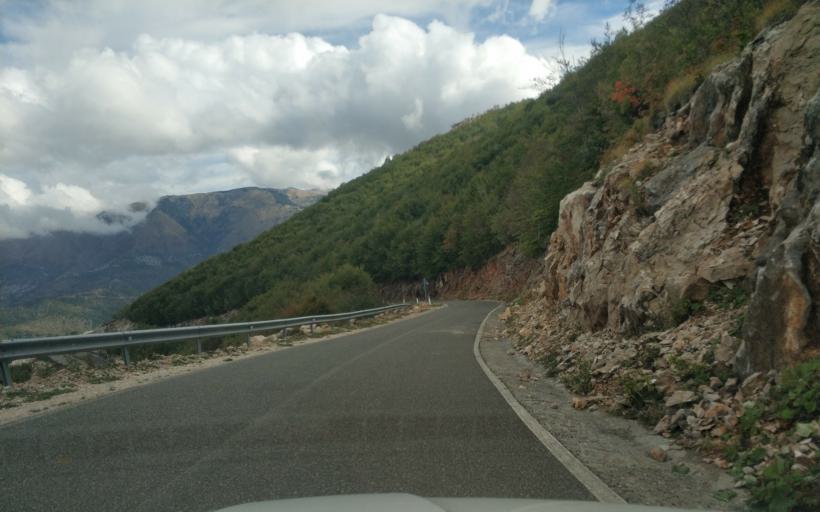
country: AL
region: Durres
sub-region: Rrethi i Krujes
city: Kruje
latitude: 41.5223
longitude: 19.8051
